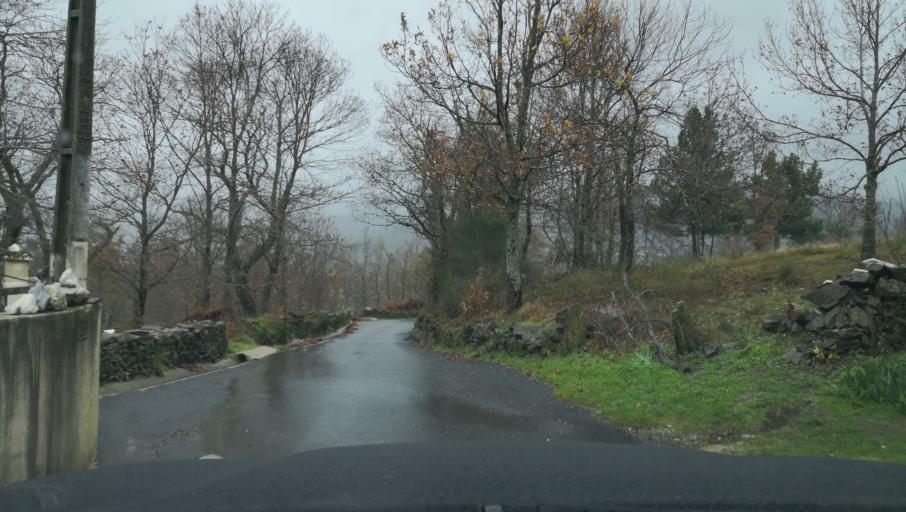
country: PT
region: Vila Real
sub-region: Santa Marta de Penaguiao
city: Santa Marta de Penaguiao
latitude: 41.2834
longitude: -7.8630
